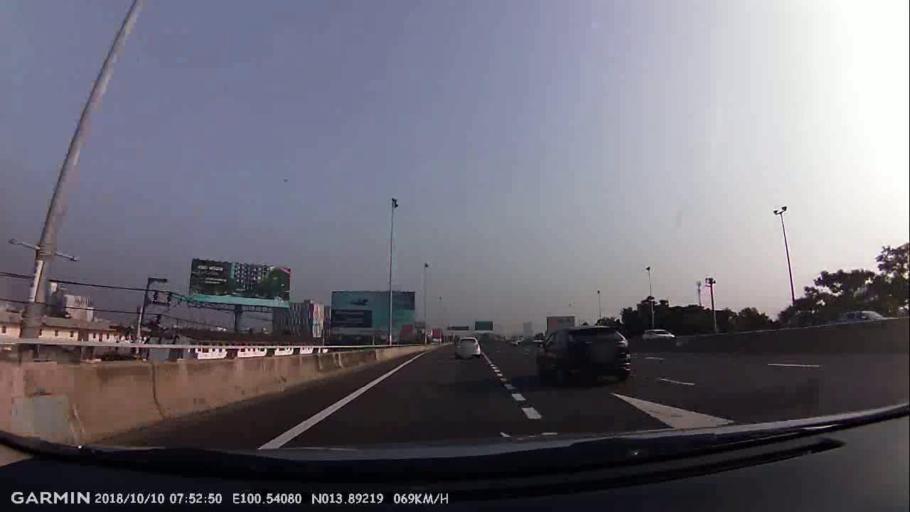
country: TH
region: Bangkok
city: Lak Si
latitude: 13.8924
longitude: 100.5408
